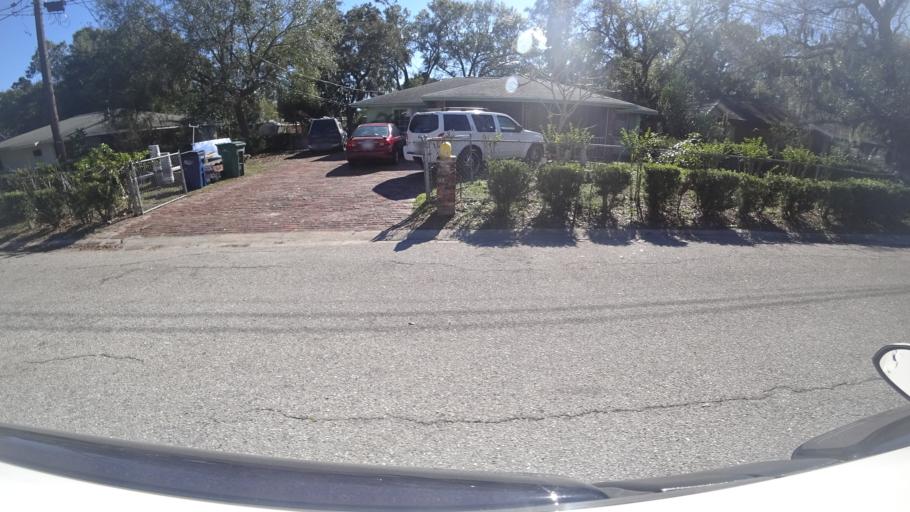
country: US
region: Florida
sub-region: Manatee County
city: Whitfield
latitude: 27.4353
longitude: -82.5539
